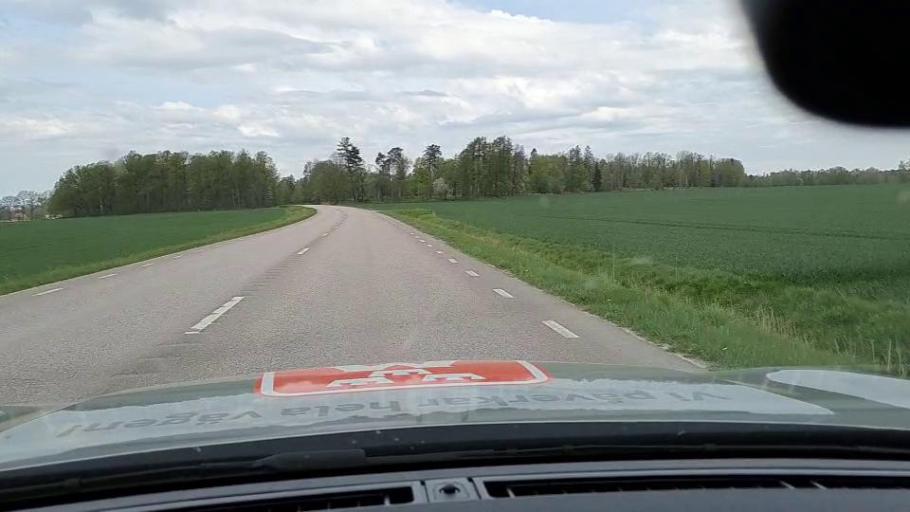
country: SE
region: Soedermanland
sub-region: Vingakers Kommun
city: Vingaker
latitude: 59.1561
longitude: 16.0297
